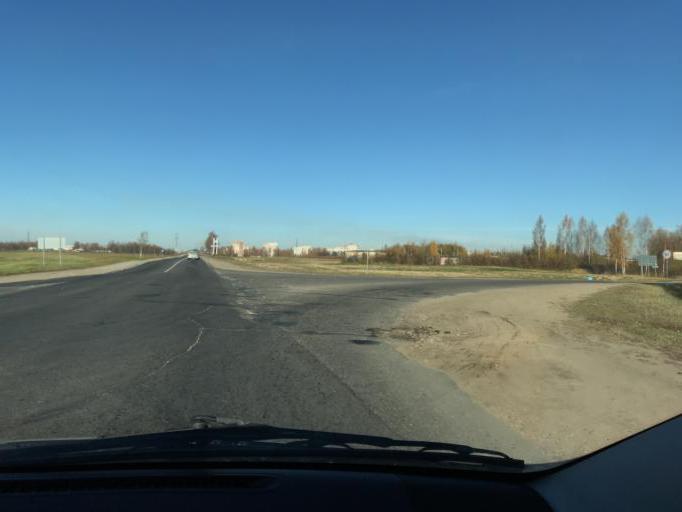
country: BY
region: Vitebsk
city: Polatsk
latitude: 55.4565
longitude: 28.7647
